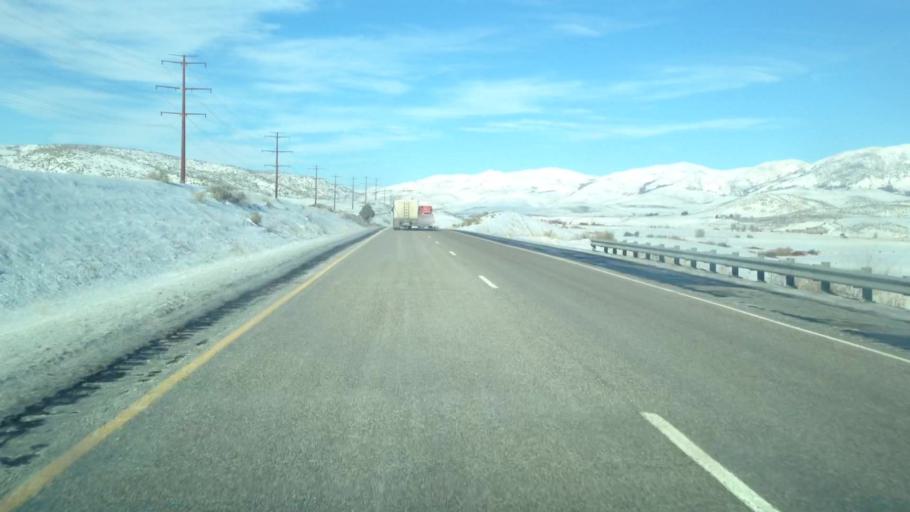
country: US
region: Idaho
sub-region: Oneida County
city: Malad City
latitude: 42.2524
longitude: -112.2218
